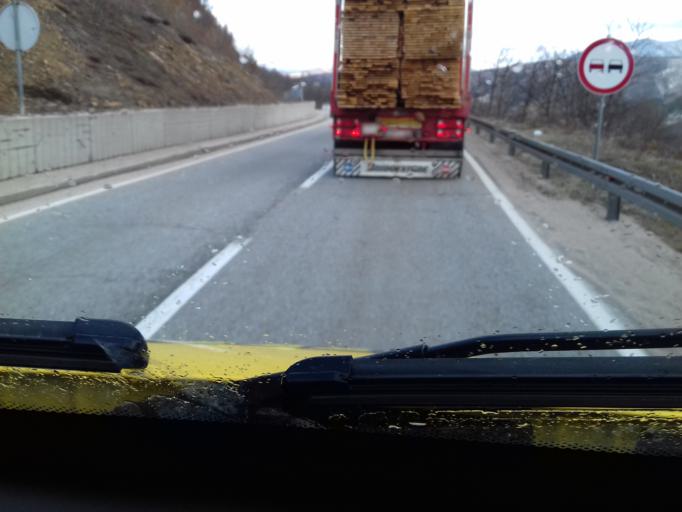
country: BA
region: Federation of Bosnia and Herzegovina
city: Novi Travnik
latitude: 44.1450
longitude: 17.5742
